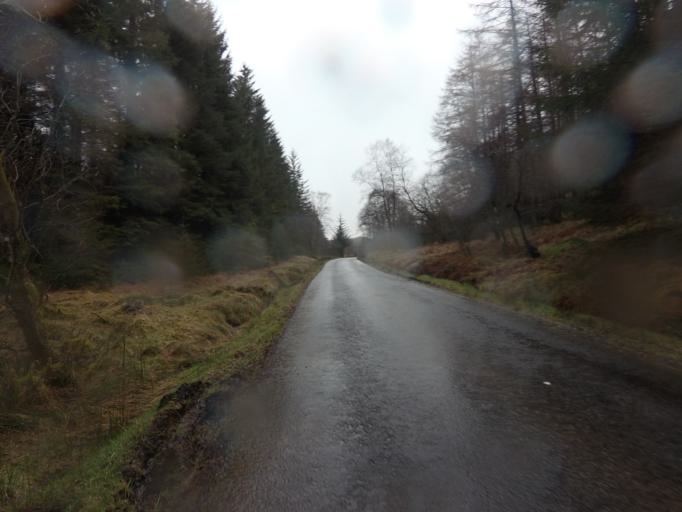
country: GB
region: Scotland
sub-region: West Dunbartonshire
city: Balloch
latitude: 56.2319
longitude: -4.5586
